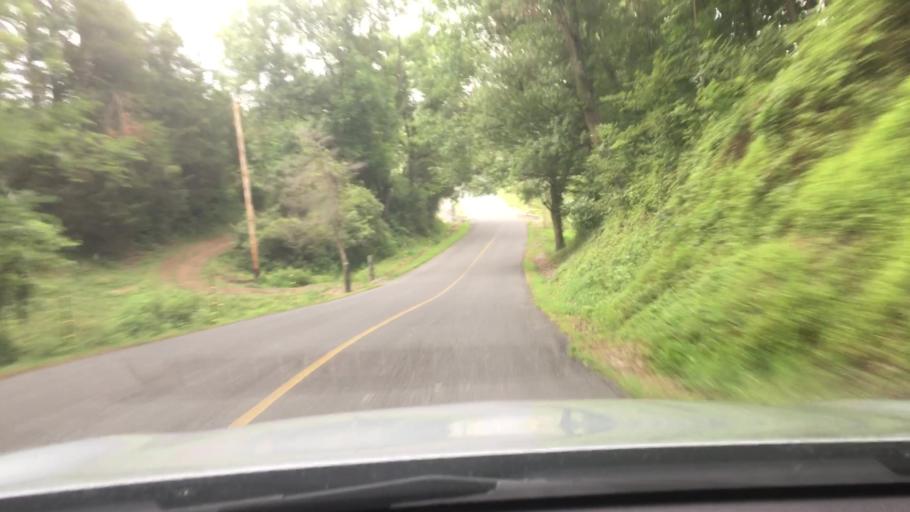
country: US
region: Pennsylvania
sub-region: Franklin County
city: Greencastle
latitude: 39.8759
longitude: -77.7931
